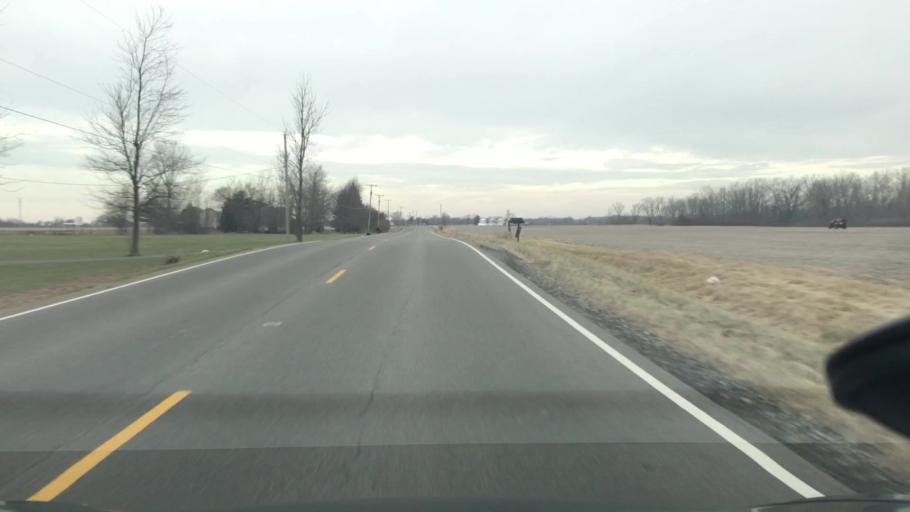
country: US
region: Ohio
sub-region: Madison County
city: London
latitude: 39.8385
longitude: -83.3813
